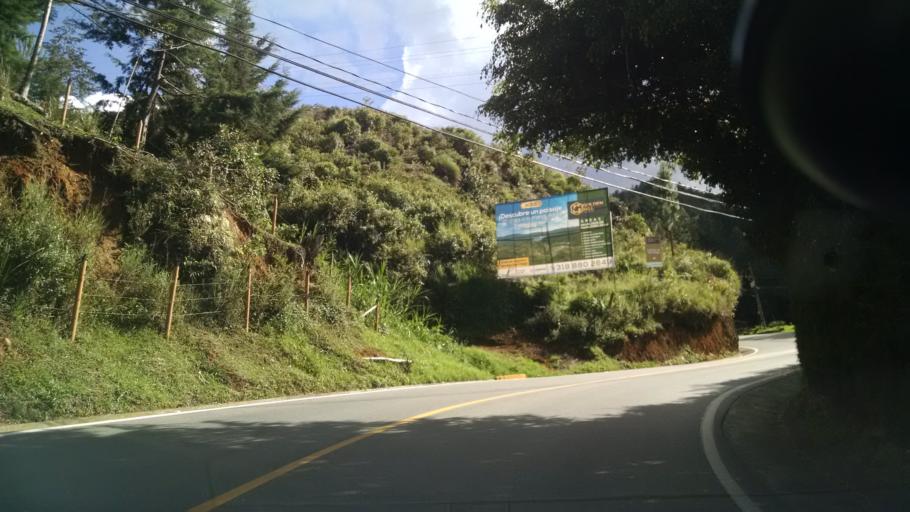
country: CO
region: Antioquia
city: El Retiro
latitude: 6.0846
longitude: -75.4772
